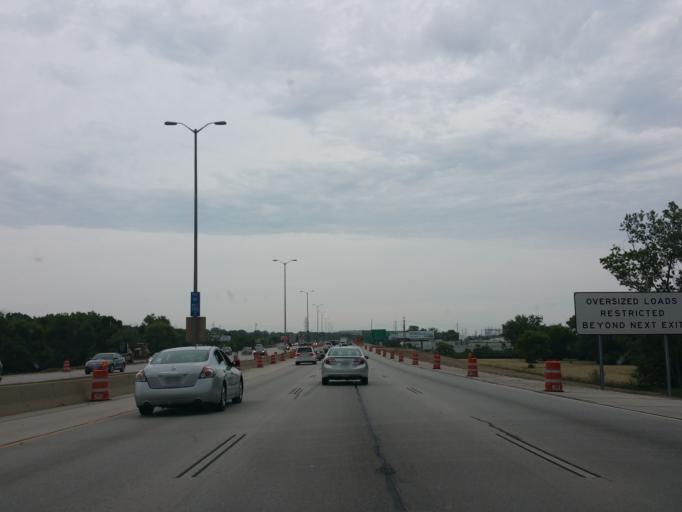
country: US
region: Wisconsin
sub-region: Waukesha County
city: Elm Grove
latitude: 43.0288
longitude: -88.0711
